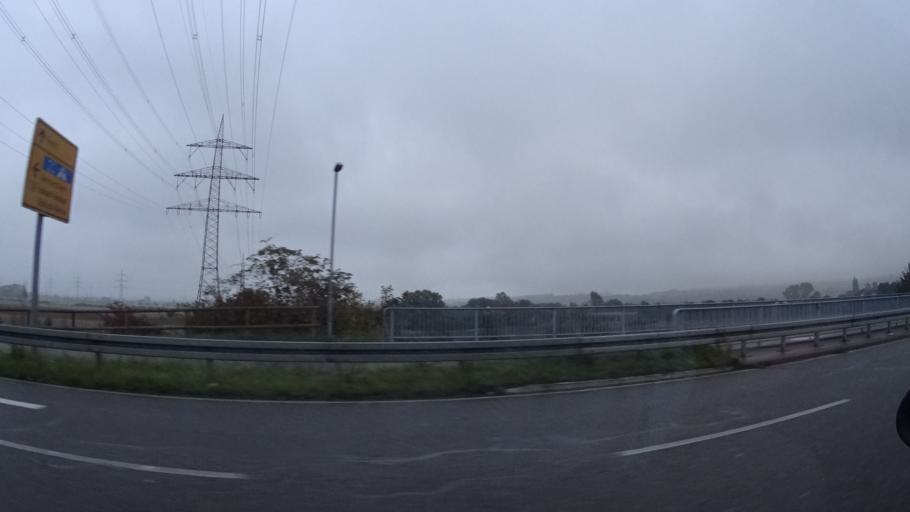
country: DE
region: Baden-Wuerttemberg
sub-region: Karlsruhe Region
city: Forst
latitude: 49.1429
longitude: 8.5897
